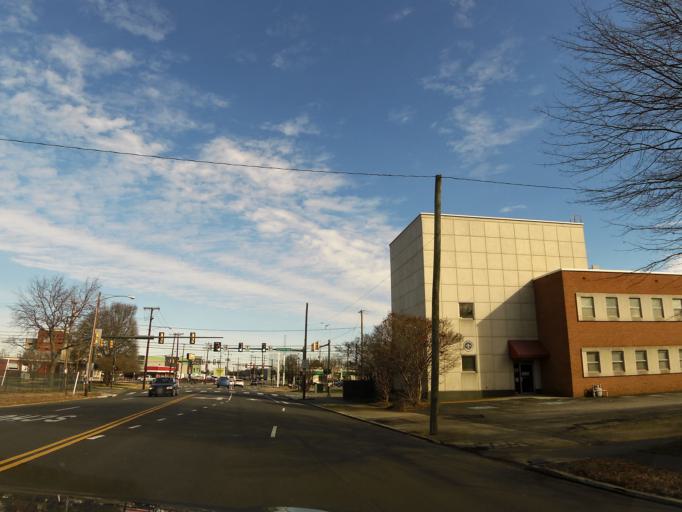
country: US
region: Virginia
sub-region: City of Richmond
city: Richmond
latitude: 37.5725
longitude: -77.4844
